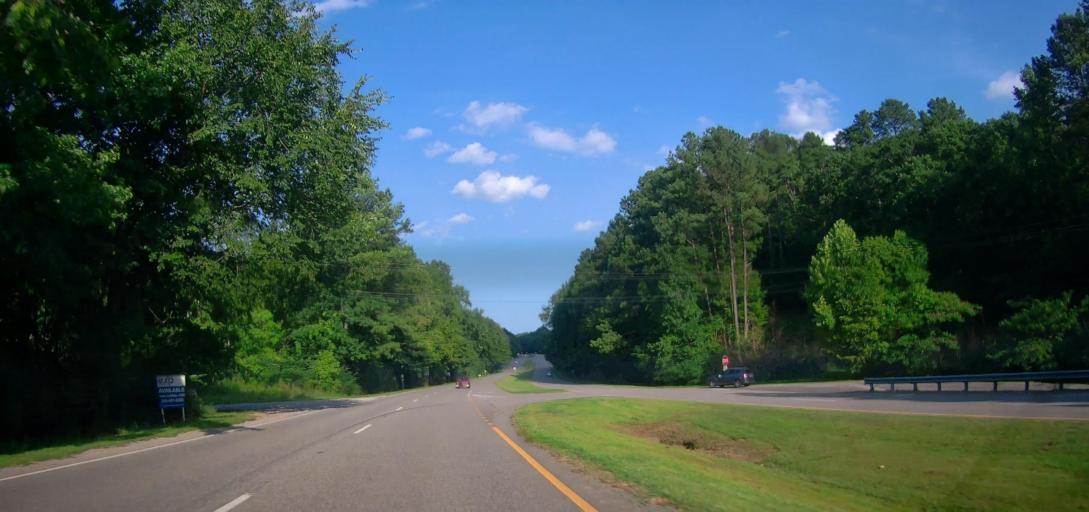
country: US
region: Alabama
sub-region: Jefferson County
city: Trussville
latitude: 33.5499
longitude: -86.6263
